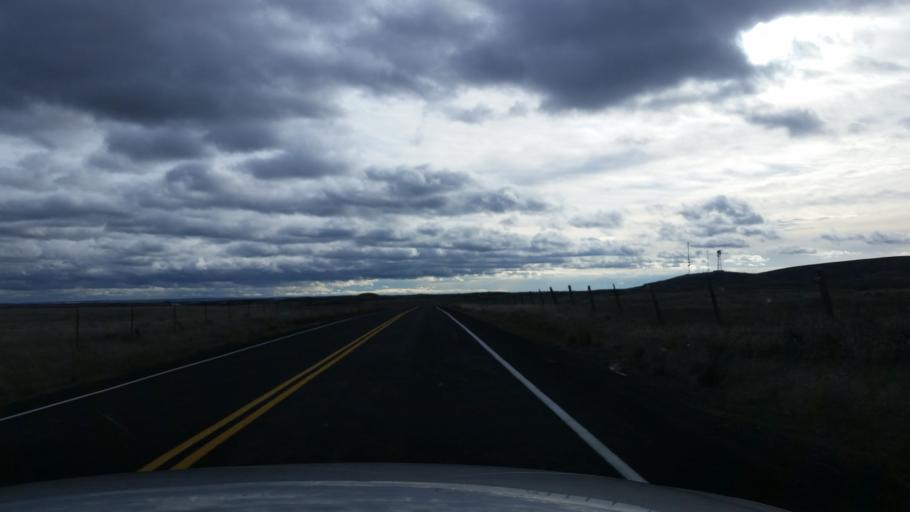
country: US
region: Washington
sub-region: Lincoln County
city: Davenport
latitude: 47.3310
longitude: -117.9833
